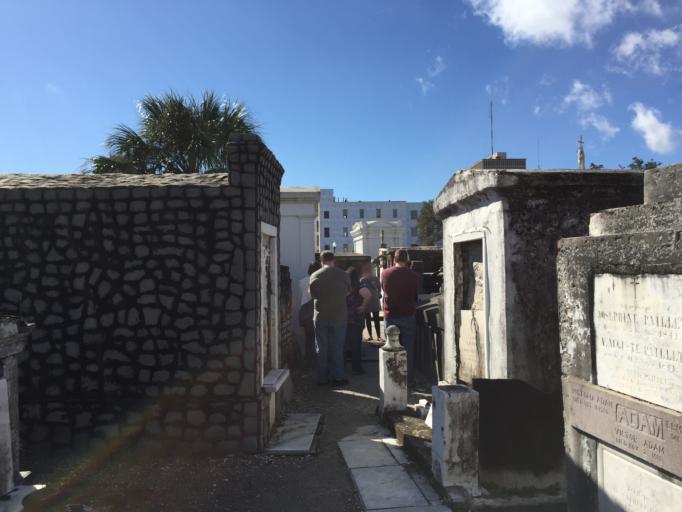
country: US
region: Louisiana
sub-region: Orleans Parish
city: New Orleans
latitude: 29.9594
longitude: -90.0712
